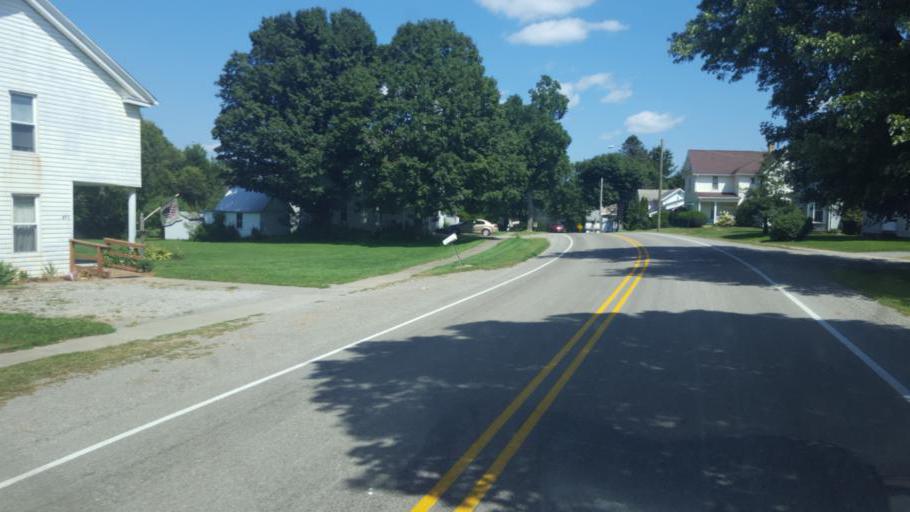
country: US
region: Pennsylvania
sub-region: Clarion County
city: Knox
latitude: 41.1259
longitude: -79.5554
